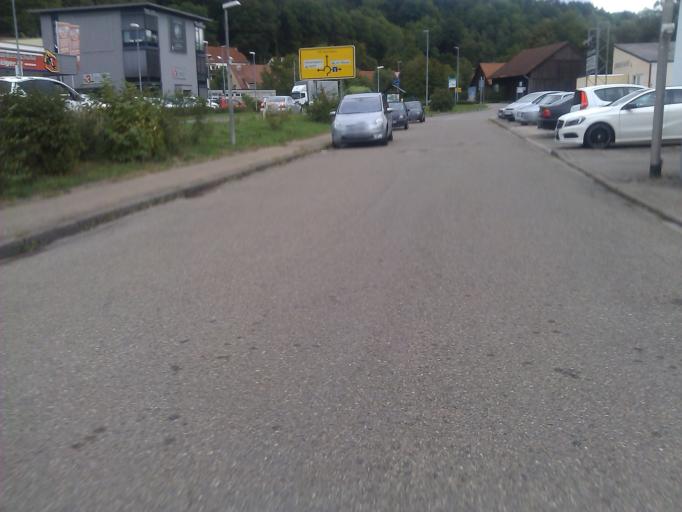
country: DE
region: Baden-Wuerttemberg
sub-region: Regierungsbezirk Stuttgart
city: Neckartenzlingen
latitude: 48.5886
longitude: 9.2299
